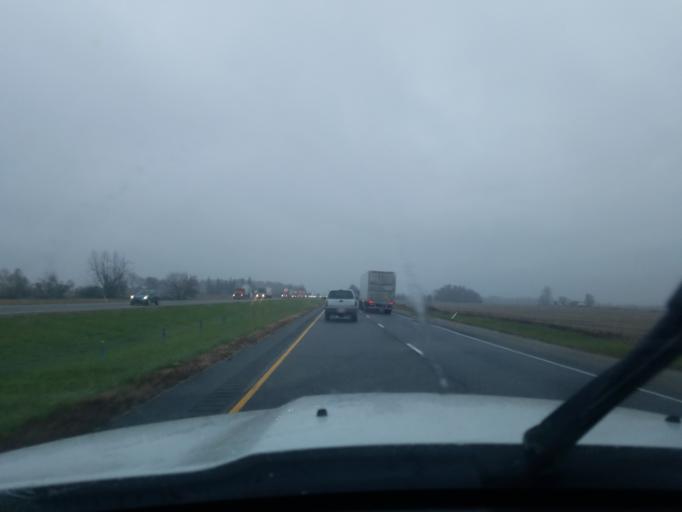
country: US
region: Indiana
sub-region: Grant County
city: Upland
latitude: 40.3955
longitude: -85.5488
